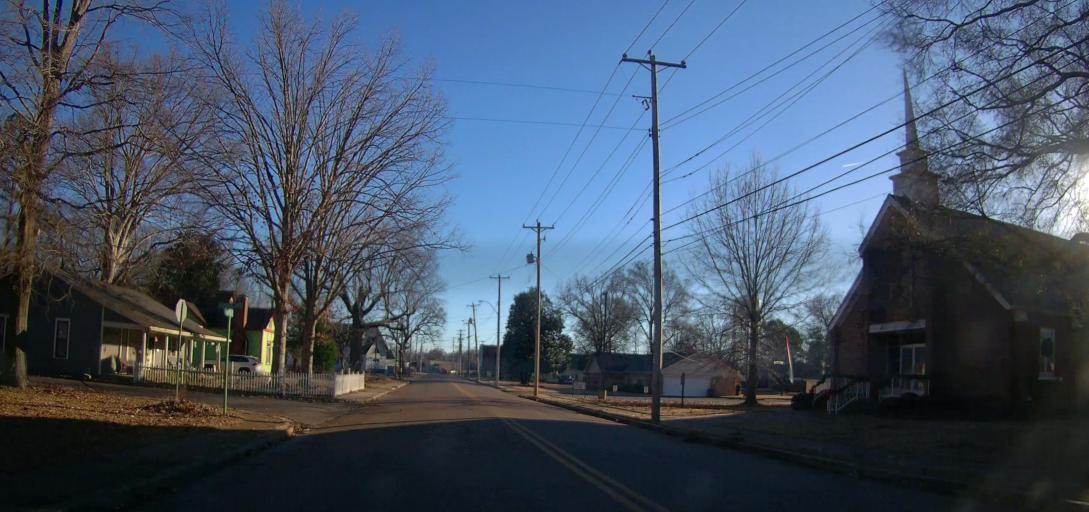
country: US
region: Tennessee
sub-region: Shelby County
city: Millington
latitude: 35.3458
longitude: -89.8945
